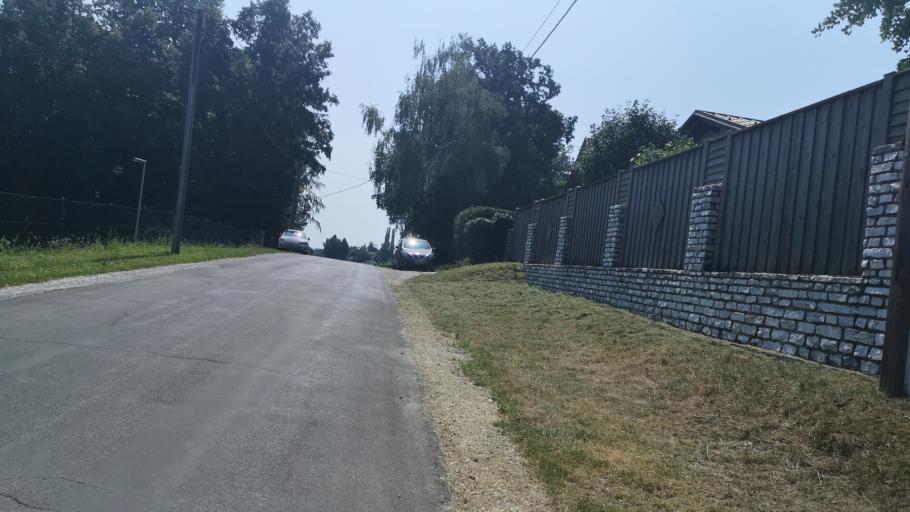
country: AT
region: Styria
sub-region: Politischer Bezirk Deutschlandsberg
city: Lannach
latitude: 46.9307
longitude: 15.3531
